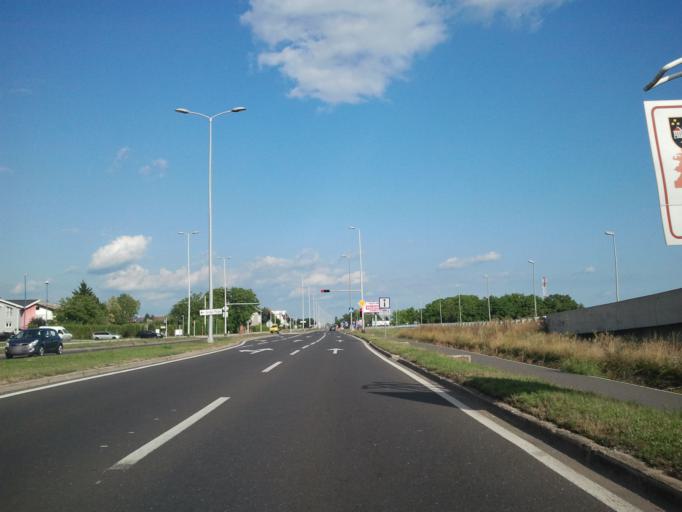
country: HR
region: Grad Zagreb
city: Odra
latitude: 45.7335
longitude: 16.0143
